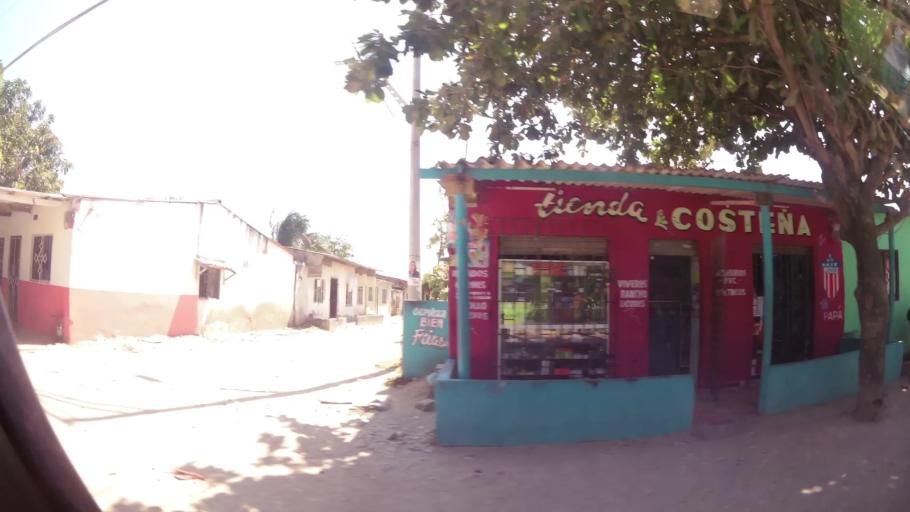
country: CO
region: Atlantico
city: Barranquilla
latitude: 10.9760
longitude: -74.8458
